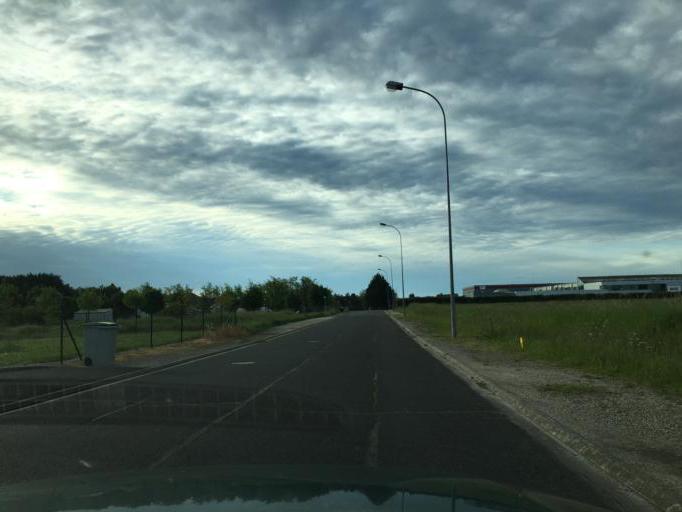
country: FR
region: Centre
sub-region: Departement du Loiret
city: Meung-sur-Loire
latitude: 47.8283
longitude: 1.6817
